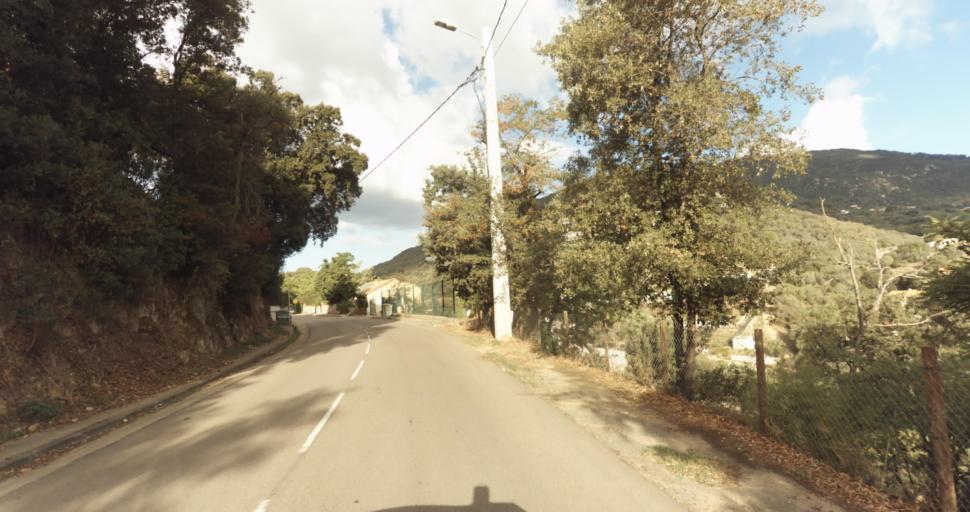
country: FR
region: Corsica
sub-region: Departement de la Corse-du-Sud
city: Ajaccio
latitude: 41.9313
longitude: 8.7228
